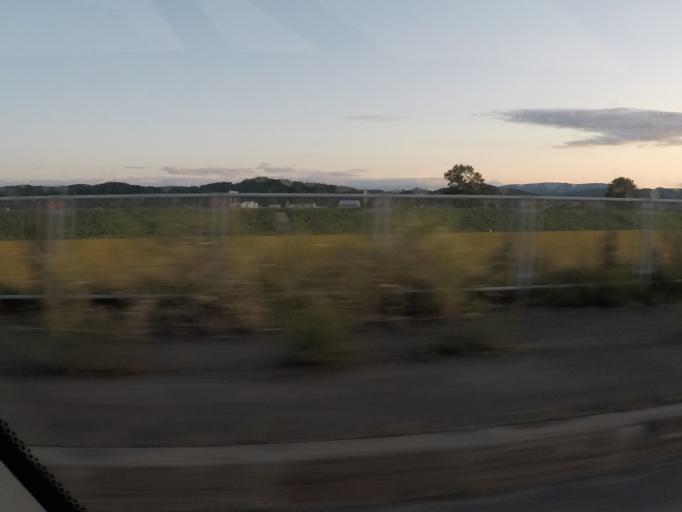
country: JP
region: Hokkaido
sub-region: Asahikawa-shi
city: Asahikawa
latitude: 43.6653
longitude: 142.4163
